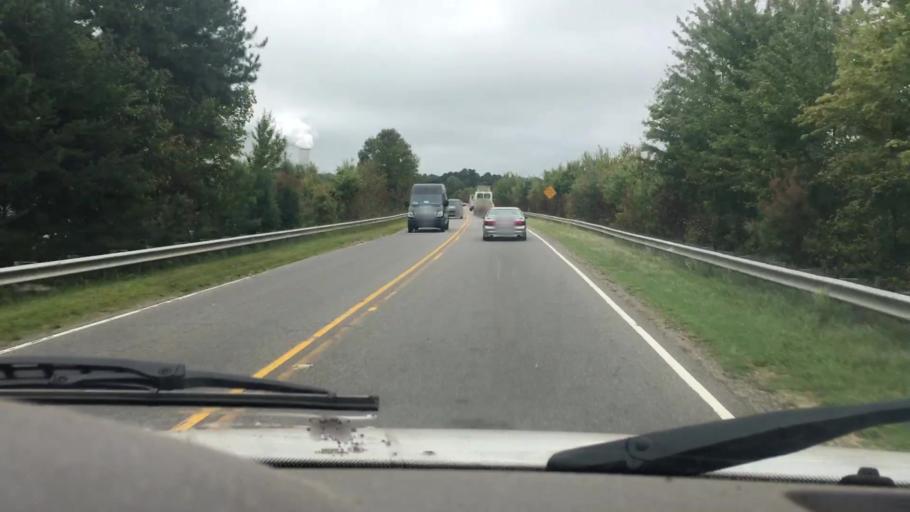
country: US
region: North Carolina
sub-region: Catawba County
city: Lake Norman of Catawba
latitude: 35.6058
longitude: -80.9390
